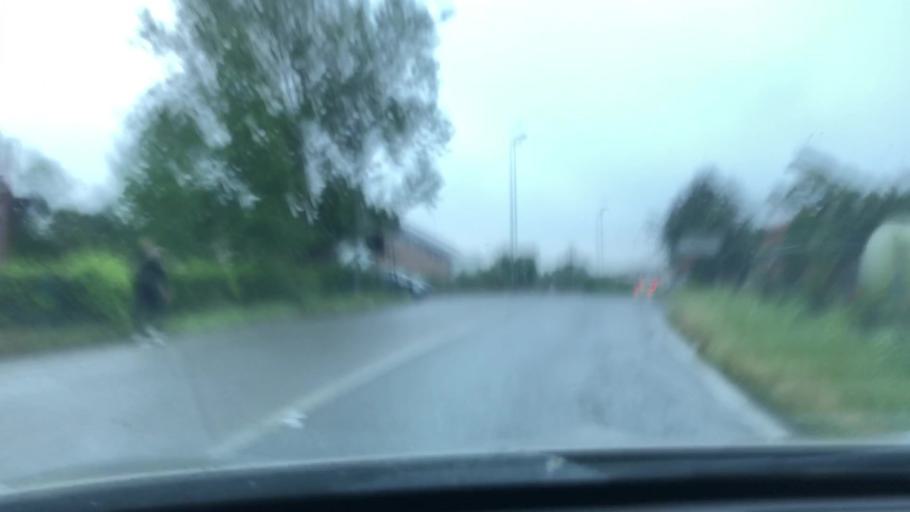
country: IT
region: Tuscany
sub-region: Province of Pisa
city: Il Romito
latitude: 43.6450
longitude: 10.6447
